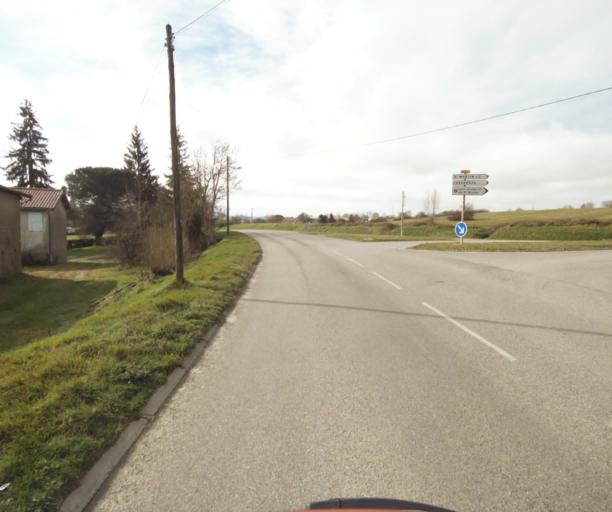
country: FR
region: Midi-Pyrenees
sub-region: Departement de l'Ariege
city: Pamiers
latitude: 43.1290
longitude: 1.5513
